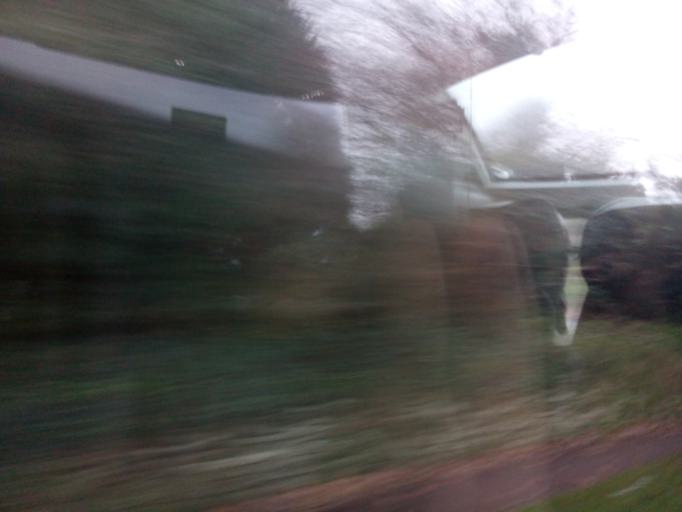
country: GB
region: England
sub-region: Cornwall
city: Liskeard
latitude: 50.4537
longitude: -4.4588
